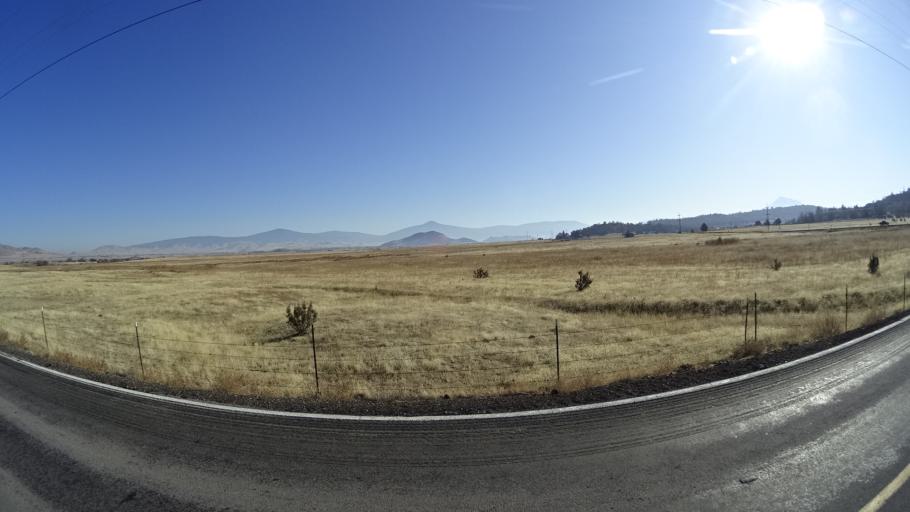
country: US
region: California
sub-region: Siskiyou County
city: Yreka
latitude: 41.7128
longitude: -122.5936
